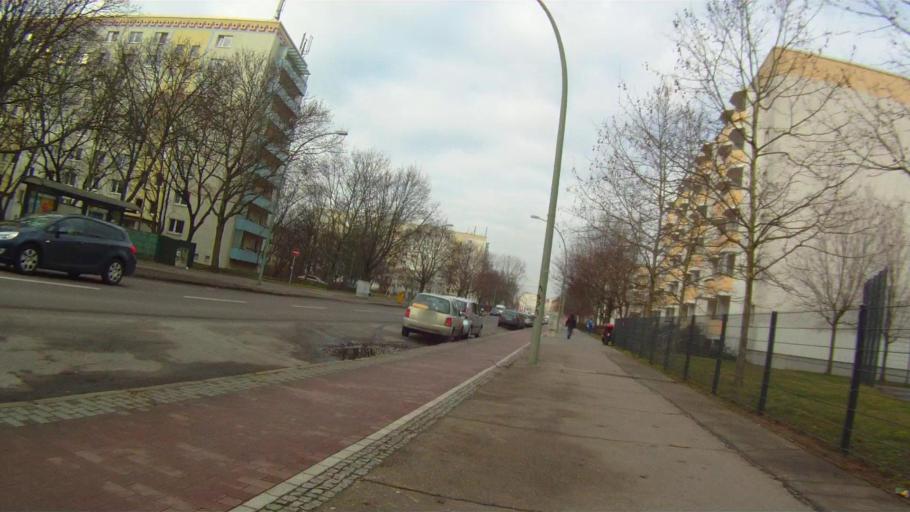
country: DE
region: Berlin
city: Rummelsburg
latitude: 52.4988
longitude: 13.5010
